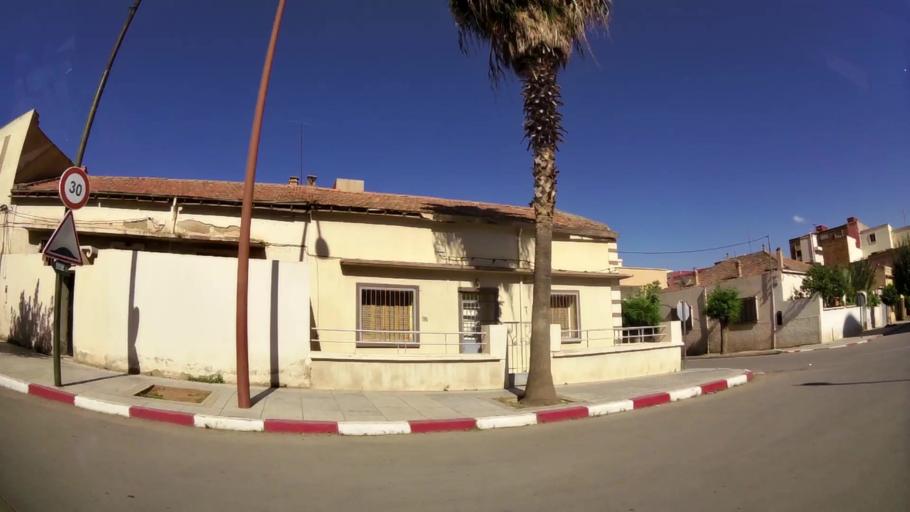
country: MA
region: Oriental
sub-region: Oujda-Angad
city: Oujda
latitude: 34.6877
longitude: -1.9194
